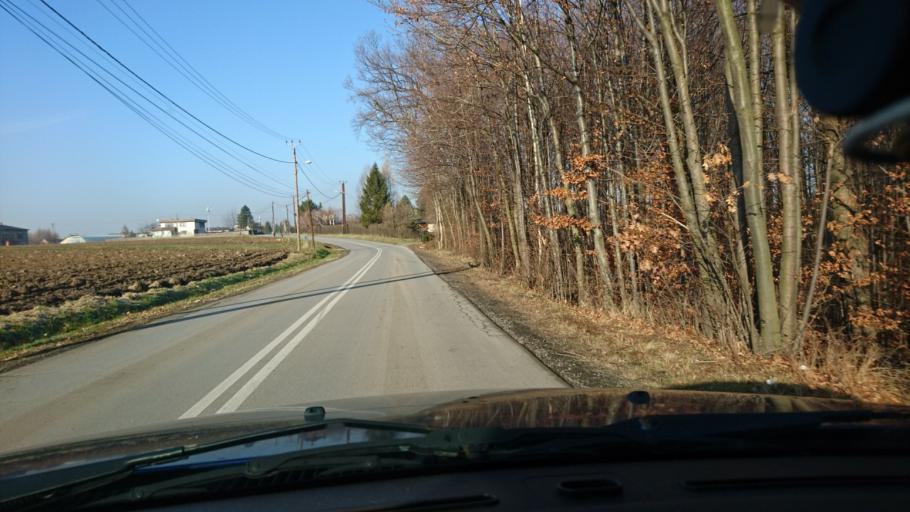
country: PL
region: Silesian Voivodeship
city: Janowice
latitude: 49.8814
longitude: 19.1008
